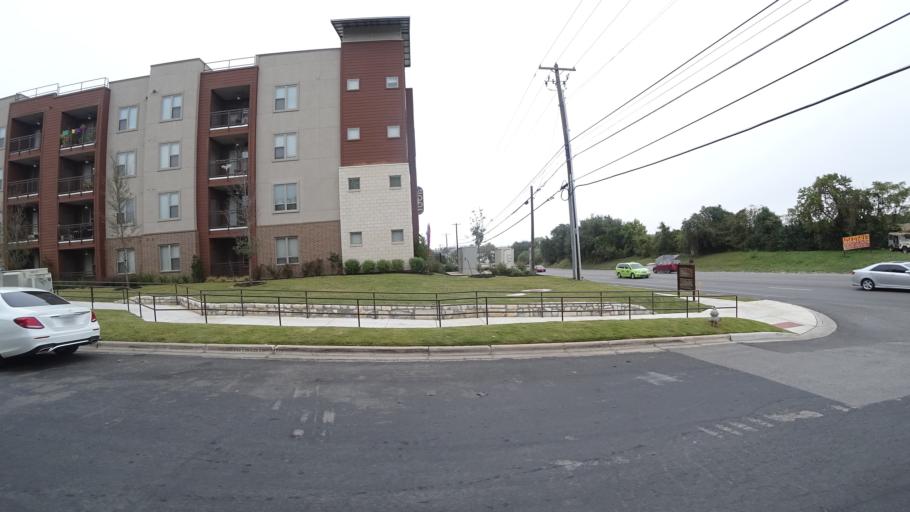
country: US
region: Texas
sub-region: Travis County
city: Austin
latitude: 30.2089
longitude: -97.7731
